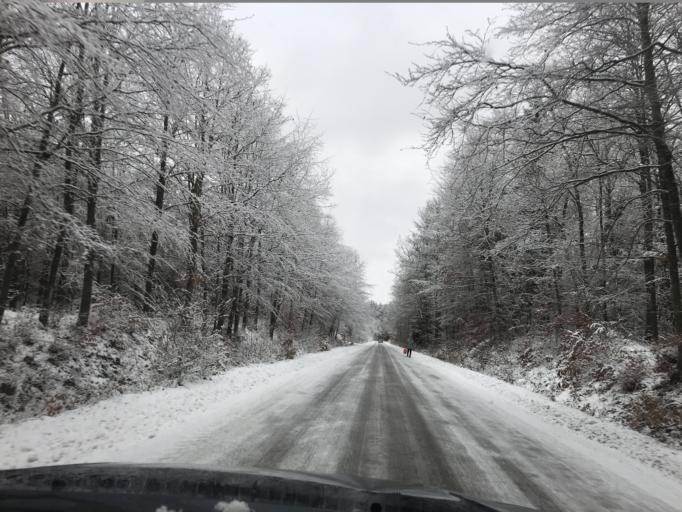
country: PL
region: Pomeranian Voivodeship
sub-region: Powiat bytowski
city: Parchowo
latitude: 54.2445
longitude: 17.5776
